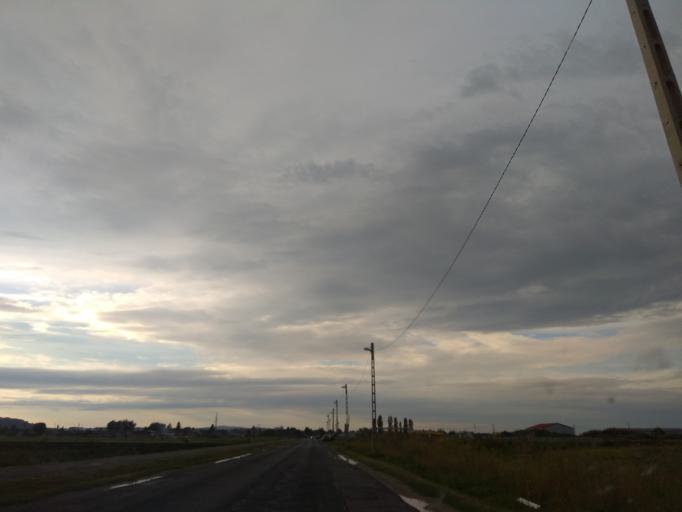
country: HU
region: Borsod-Abauj-Zemplen
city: Miskolc
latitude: 48.0802
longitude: 20.8216
